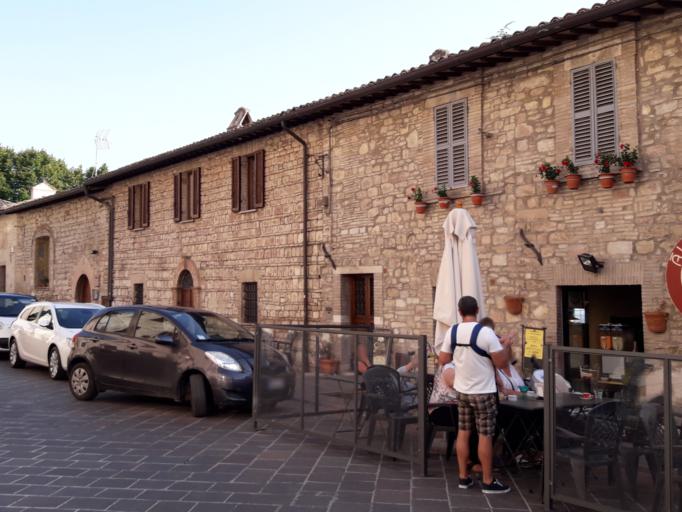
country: IT
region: Umbria
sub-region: Provincia di Perugia
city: Assisi
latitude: 43.0676
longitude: 12.6188
